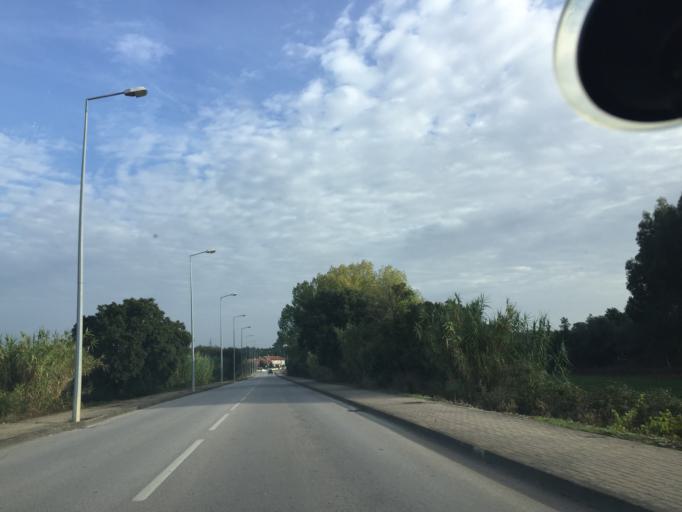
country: PT
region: Aveiro
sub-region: Anadia
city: Arcos
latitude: 40.4500
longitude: -8.4359
